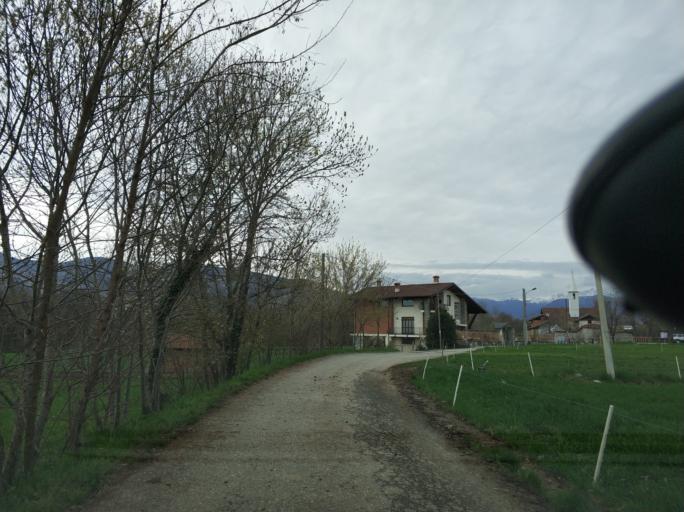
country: IT
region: Piedmont
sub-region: Provincia di Torino
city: Nole
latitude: 45.2322
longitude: 7.5627
